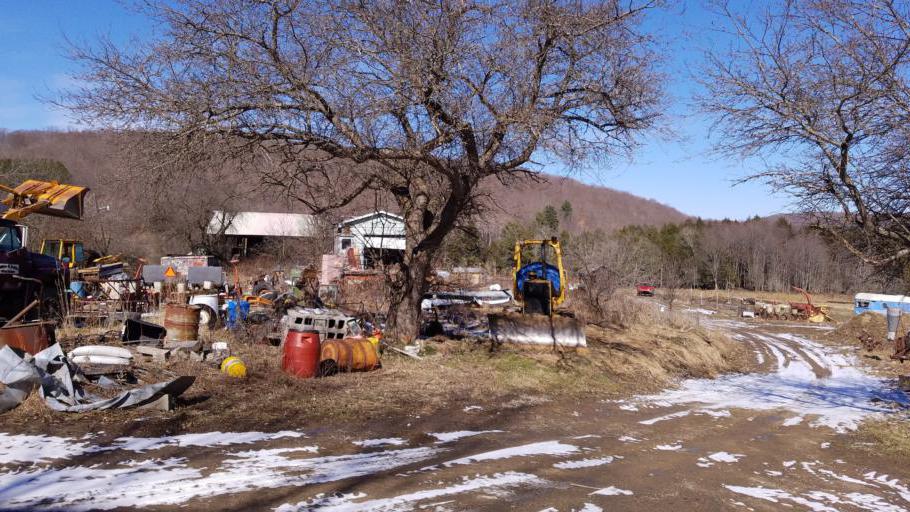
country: US
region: New York
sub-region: Allegany County
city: Wellsville
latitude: 42.0227
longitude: -77.9214
